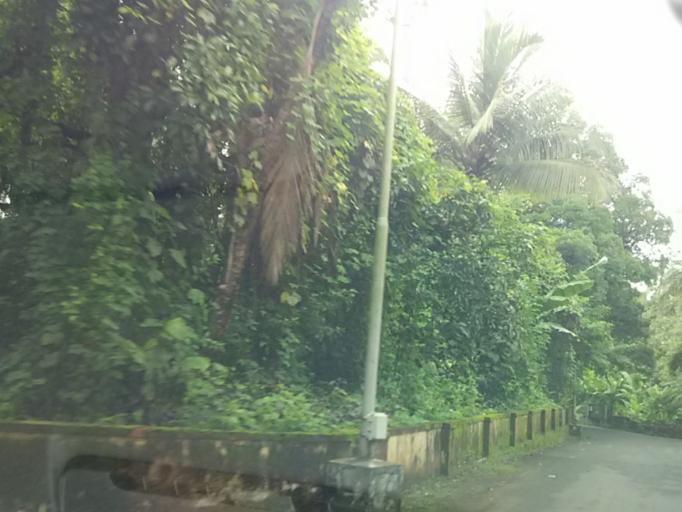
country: IN
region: Kerala
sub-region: Kozhikode
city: Mavoor
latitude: 11.3191
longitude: 75.9321
